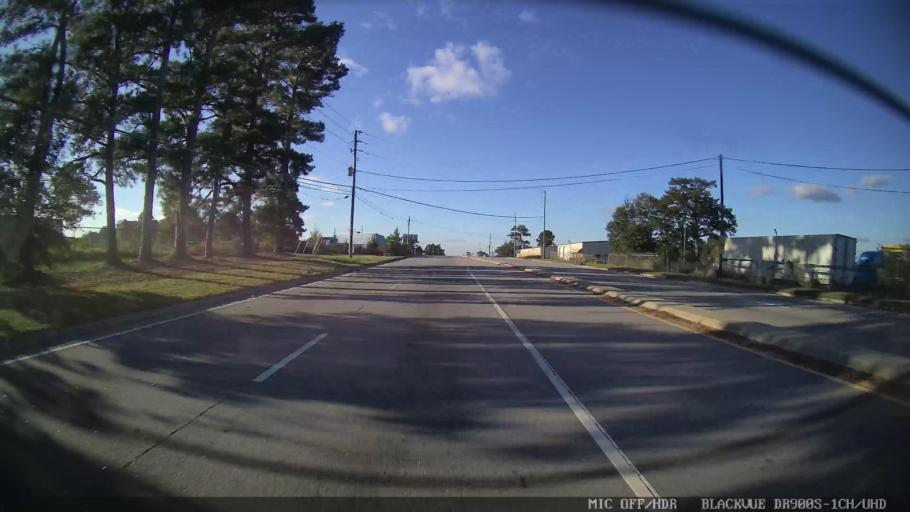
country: US
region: Georgia
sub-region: Clayton County
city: Conley
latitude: 33.6310
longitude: -84.3149
